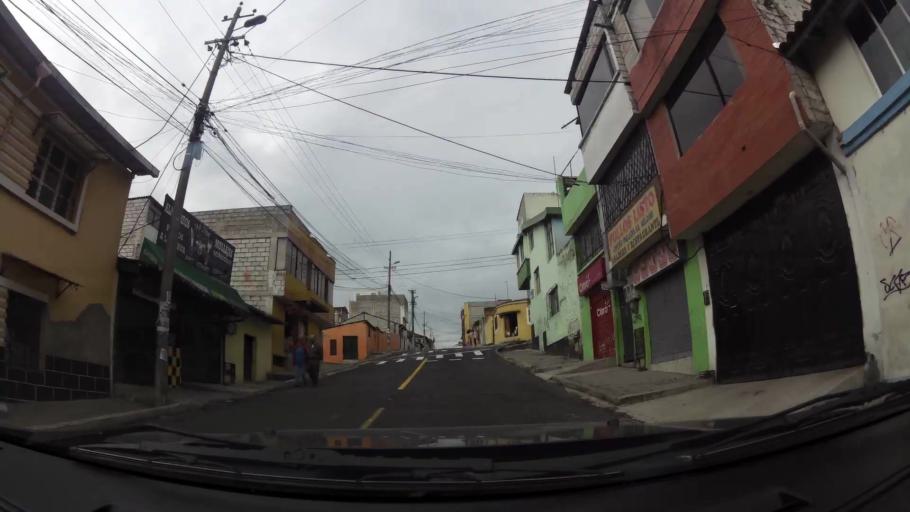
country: EC
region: Pichincha
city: Quito
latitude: -0.2099
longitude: -78.5100
